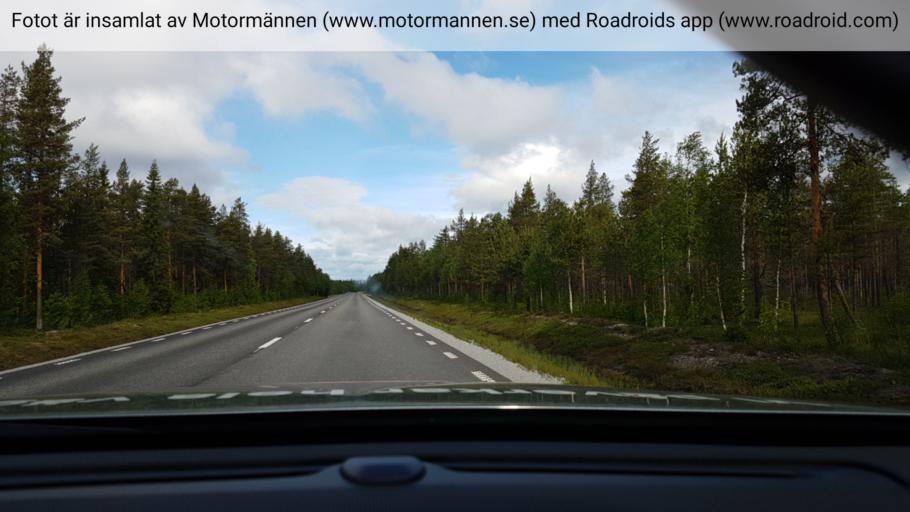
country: SE
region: Vaesternorrland
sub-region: OErnskoeldsviks Kommun
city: Bredbyn
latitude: 64.1041
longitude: 18.1475
